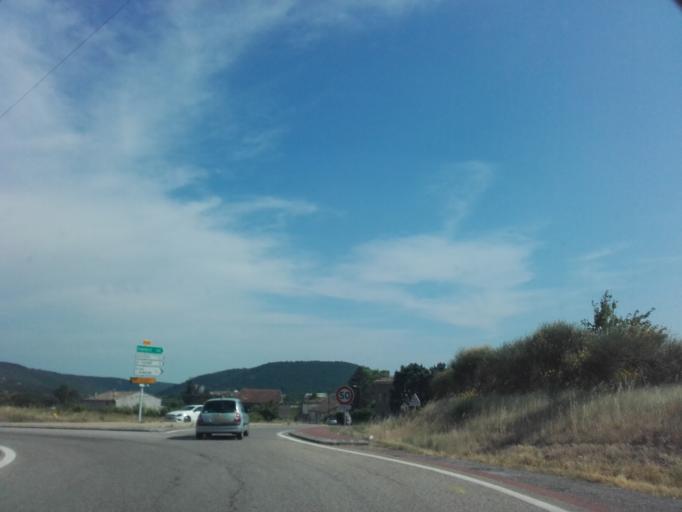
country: FR
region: Rhone-Alpes
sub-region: Departement de l'Ardeche
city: Alba-la-Romaine
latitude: 44.5679
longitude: 4.5895
